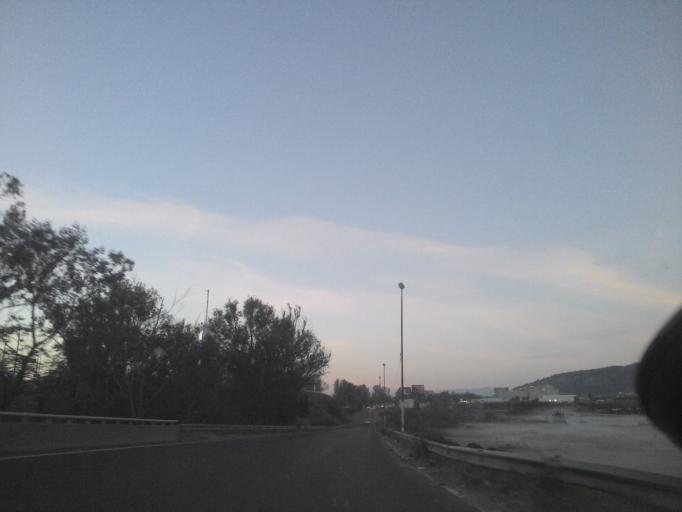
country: MX
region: Jalisco
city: Zapopan2
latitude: 20.6978
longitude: -103.4570
